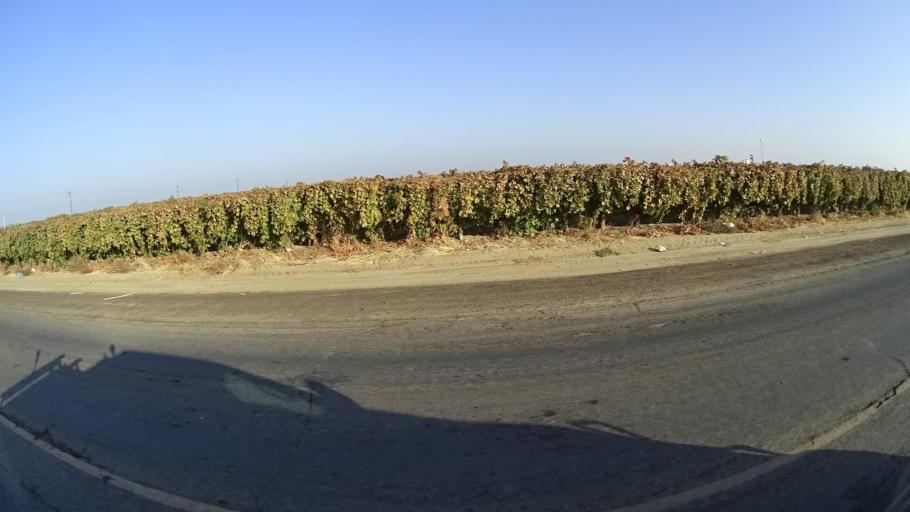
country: US
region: California
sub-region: Tulare County
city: Richgrove
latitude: 35.7906
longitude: -119.1596
